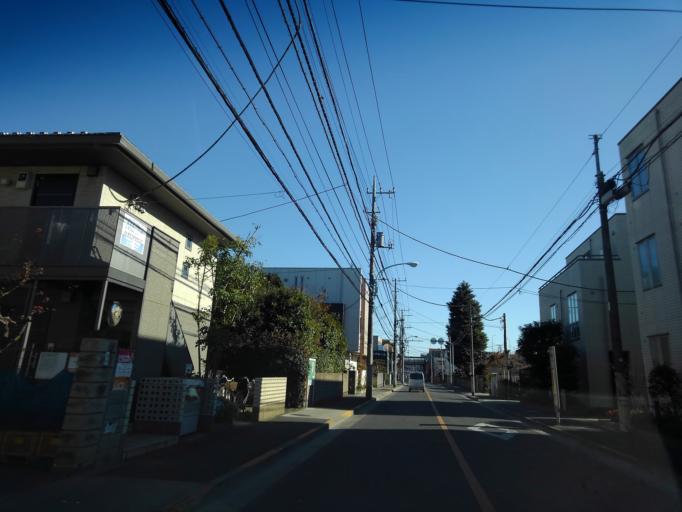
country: JP
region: Tokyo
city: Chofugaoka
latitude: 35.6599
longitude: 139.5274
